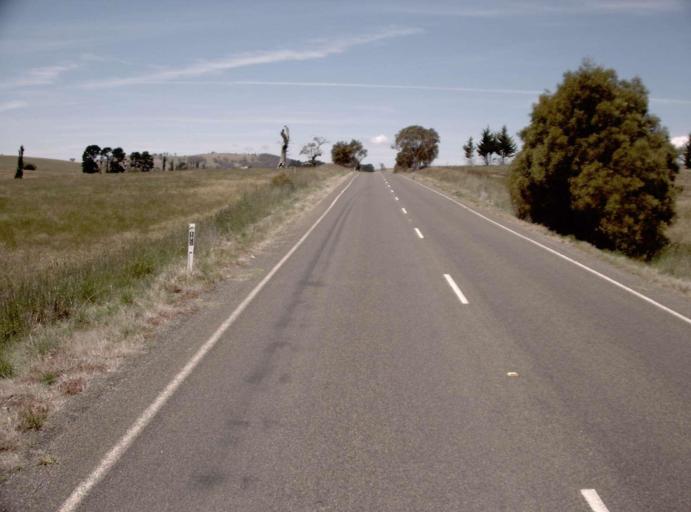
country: AU
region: Victoria
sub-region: Alpine
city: Mount Beauty
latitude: -37.1359
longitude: 147.6458
